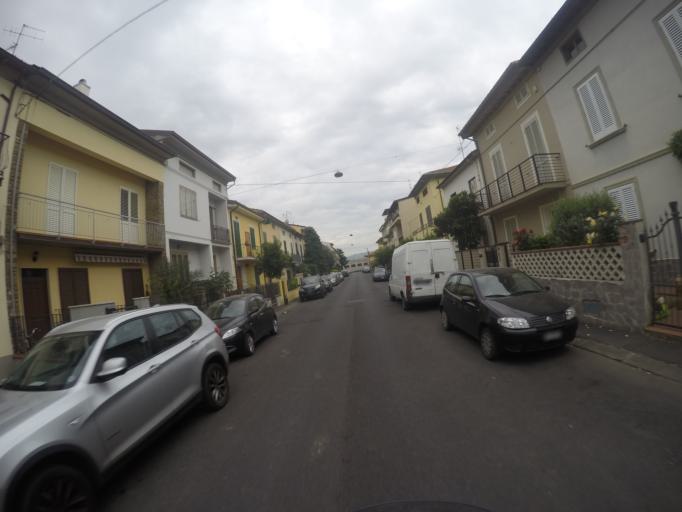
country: IT
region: Tuscany
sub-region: Provincia di Prato
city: Prato
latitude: 43.8942
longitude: 11.0715
